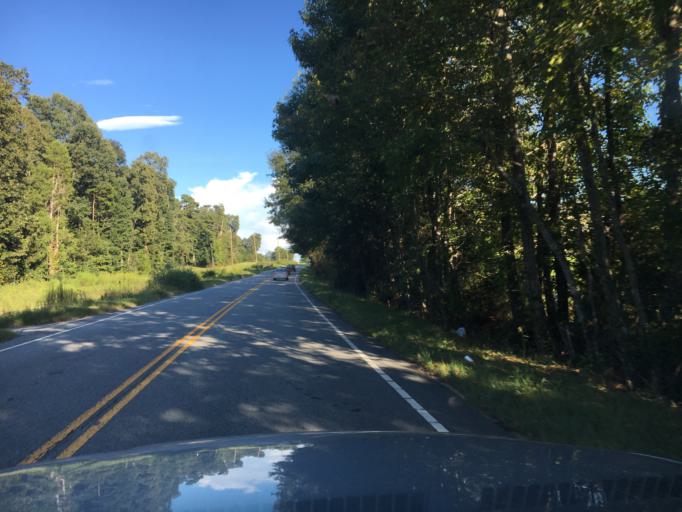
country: US
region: South Carolina
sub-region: Spartanburg County
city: Woodruff
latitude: 34.7896
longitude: -82.1194
